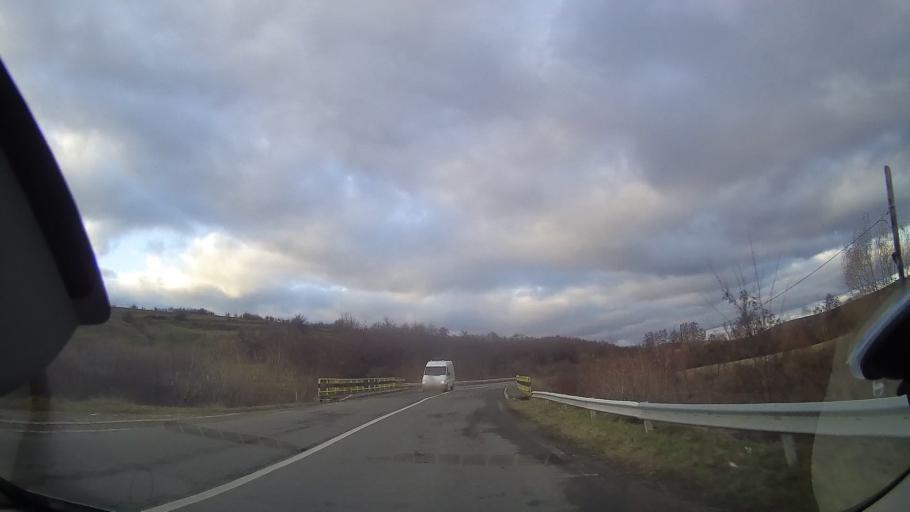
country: RO
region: Cluj
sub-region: Comuna Calatele
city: Calatele
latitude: 46.7956
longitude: 22.9947
